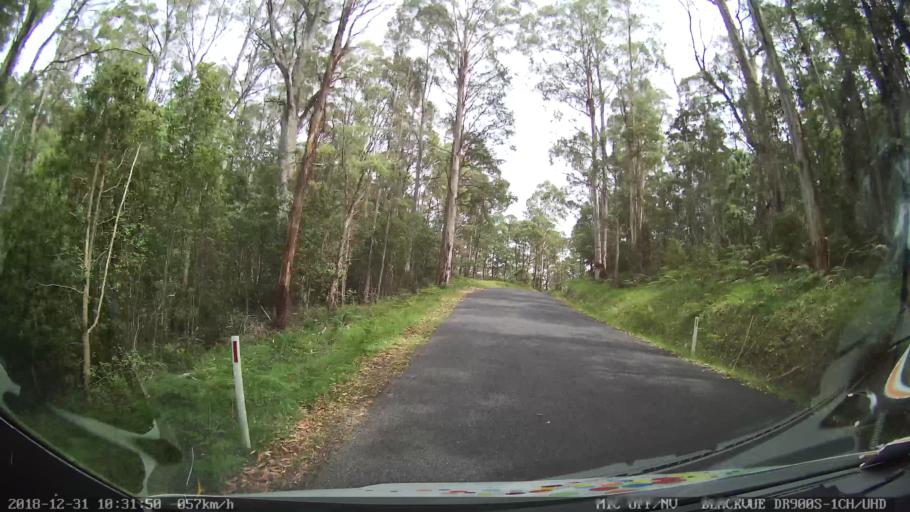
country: AU
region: New South Wales
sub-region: Snowy River
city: Jindabyne
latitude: -36.4551
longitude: 148.1598
